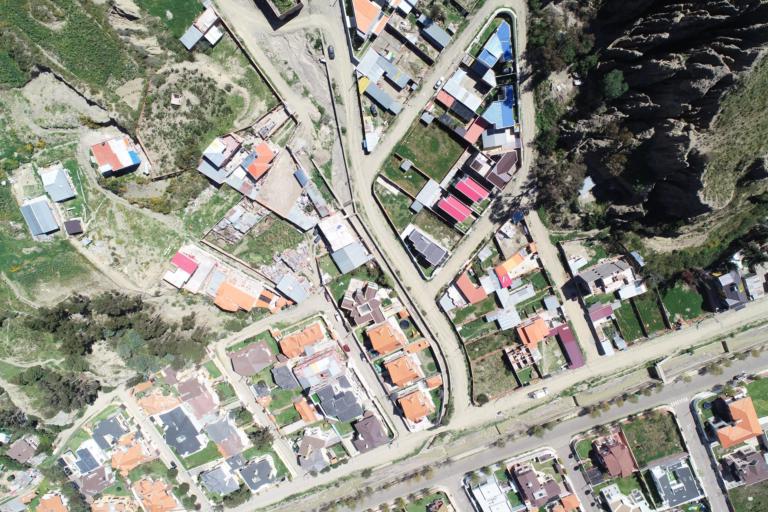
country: BO
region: La Paz
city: La Paz
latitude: -16.5090
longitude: -68.0573
